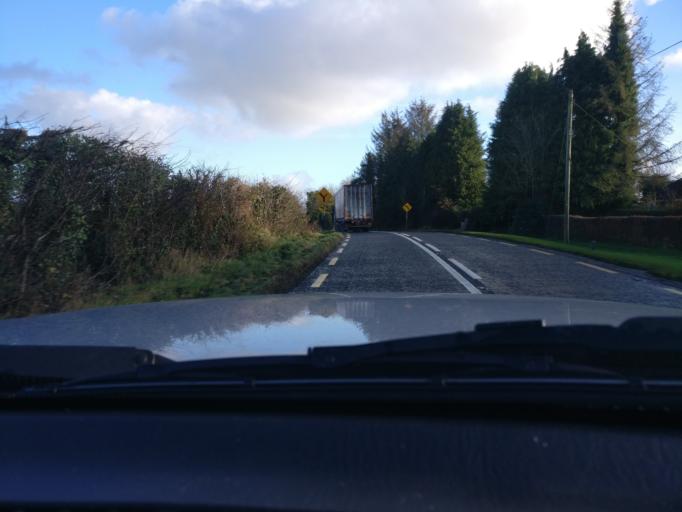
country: IE
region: Leinster
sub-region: An Iarmhi
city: Rathwire
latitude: 53.6250
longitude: -7.0680
